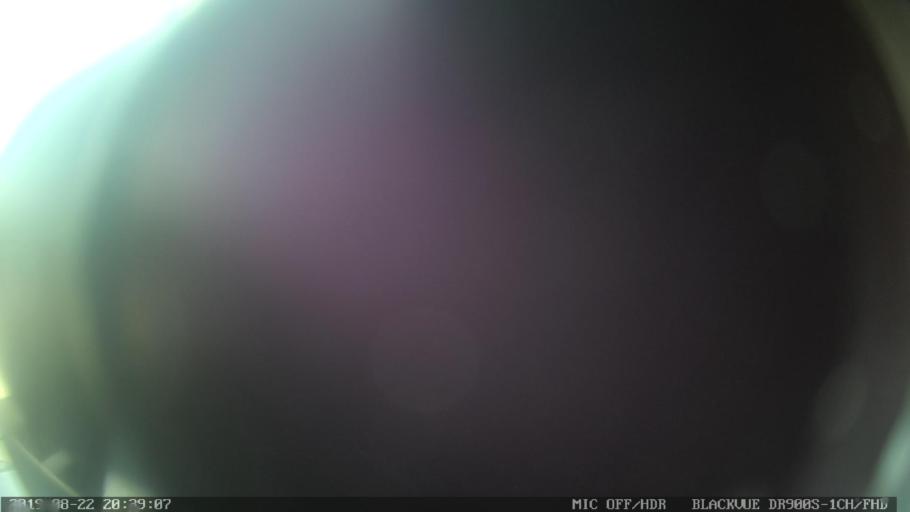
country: PT
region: Castelo Branco
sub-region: Proenca-A-Nova
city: Proenca-a-Nova
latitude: 39.6879
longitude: -7.7630
